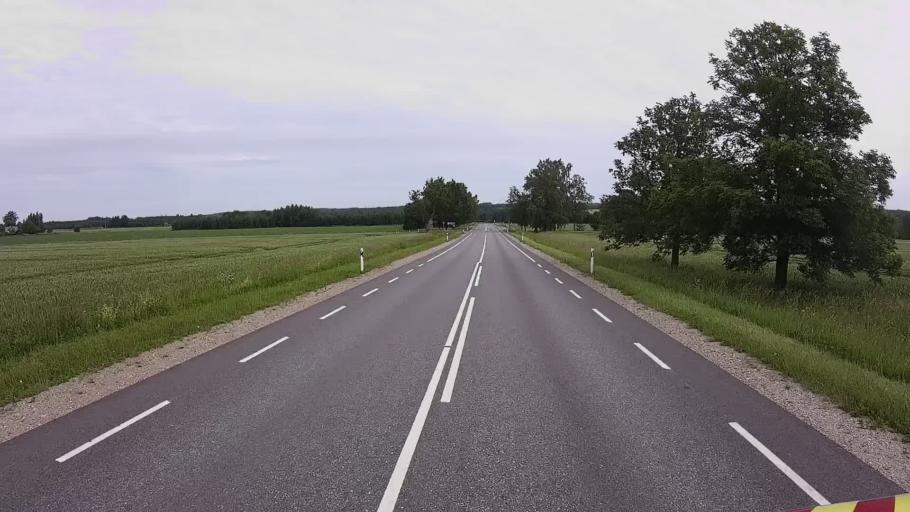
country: EE
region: Viljandimaa
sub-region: Karksi vald
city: Karksi-Nuia
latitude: 58.1377
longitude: 25.5852
